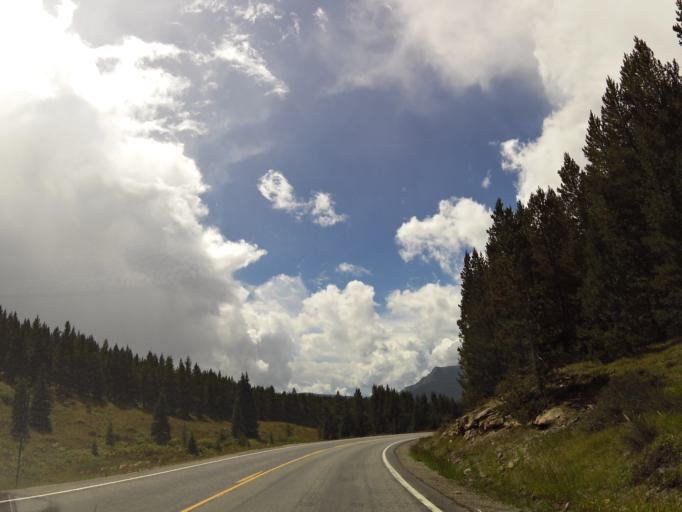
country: US
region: Colorado
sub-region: San Juan County
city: Silverton
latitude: 37.7331
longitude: -107.7178
